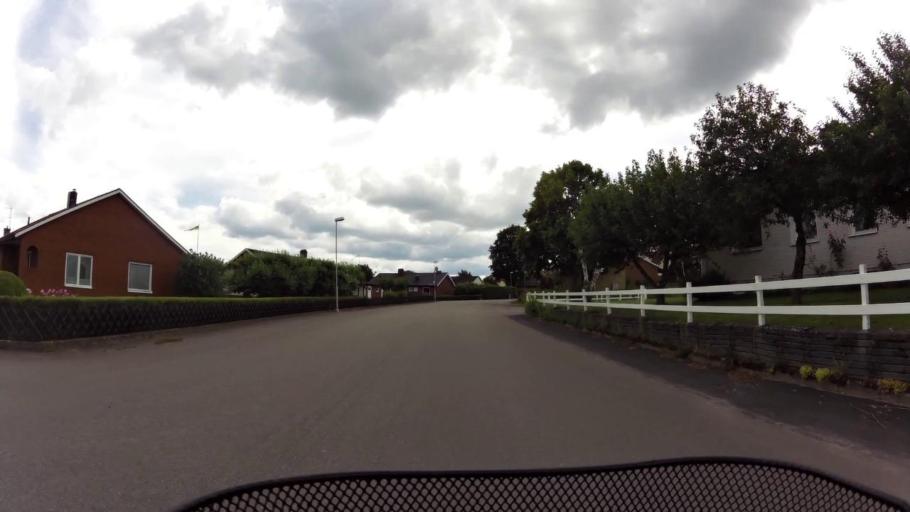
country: SE
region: OEstergoetland
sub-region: Linkopings Kommun
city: Malmslatt
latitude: 58.4183
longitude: 15.5179
